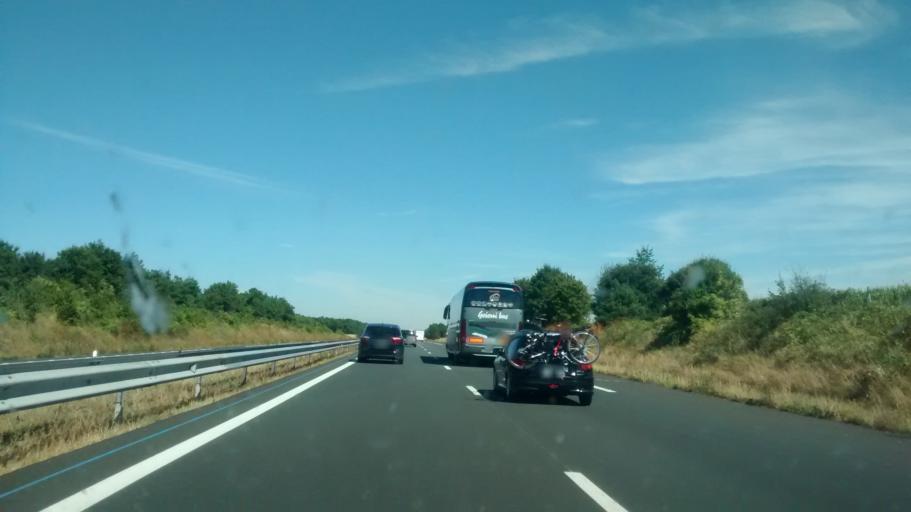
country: FR
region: Poitou-Charentes
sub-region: Departement des Deux-Sevres
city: Beauvoir-sur-Niort
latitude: 46.1853
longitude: -0.4953
